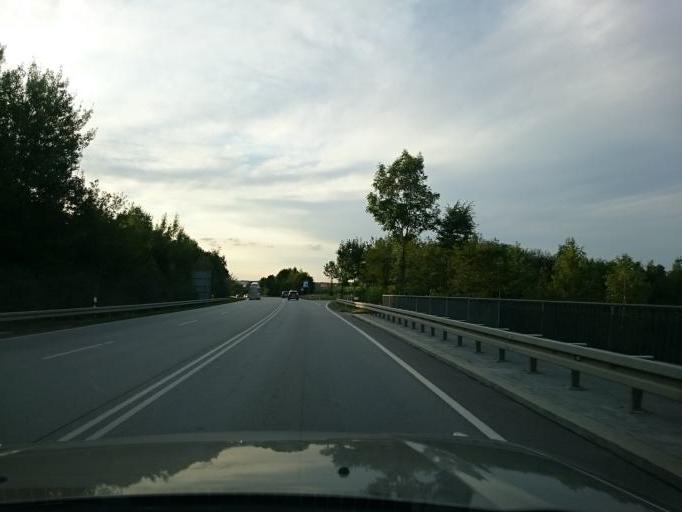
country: DE
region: Bavaria
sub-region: Lower Bavaria
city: Landau an der Isar
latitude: 48.6556
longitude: 12.7039
